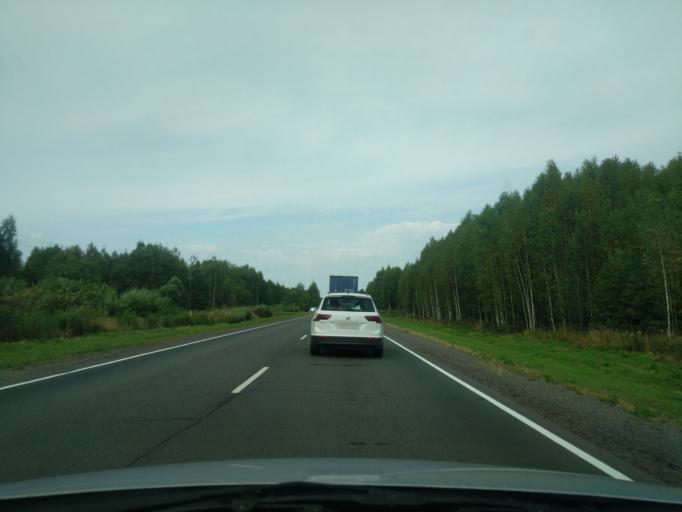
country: RU
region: Kirov
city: Leninskoye
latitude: 58.2850
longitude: 47.2501
